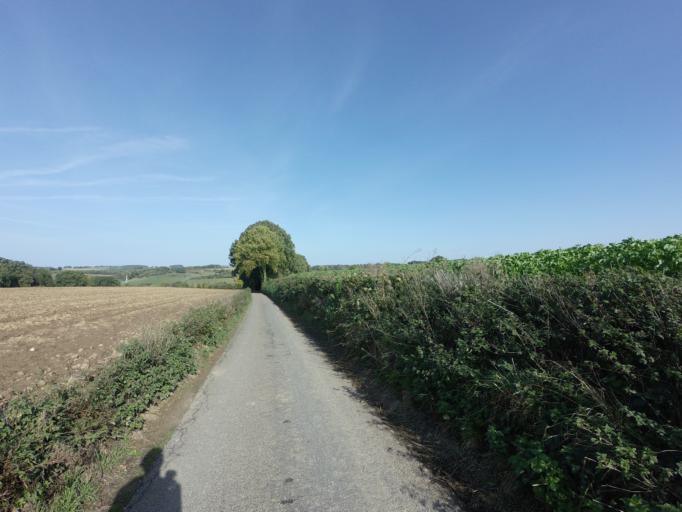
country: NL
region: Limburg
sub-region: Gemeente Simpelveld
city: Simpelveld
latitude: 50.8027
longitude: 5.9519
